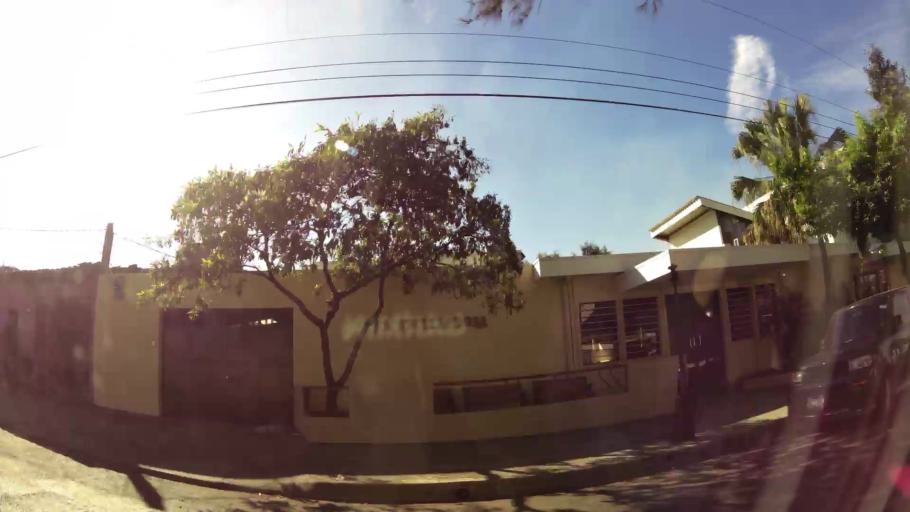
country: SV
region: Santa Ana
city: Santa Ana
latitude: 13.9940
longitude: -89.5639
